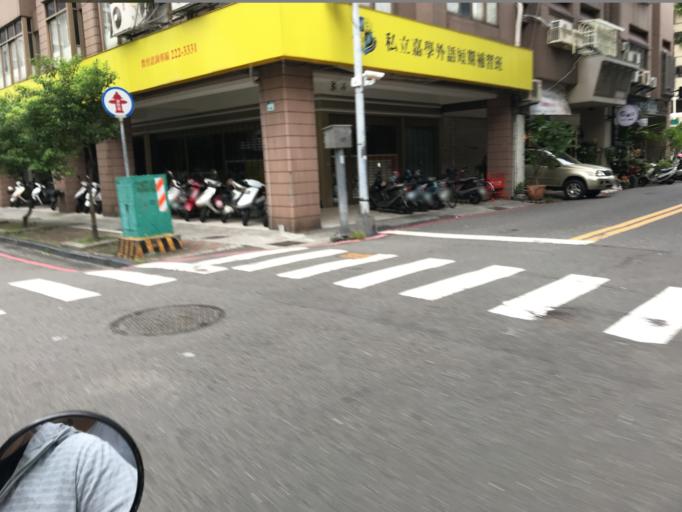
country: TW
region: Kaohsiung
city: Kaohsiung
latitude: 22.6247
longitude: 120.3153
